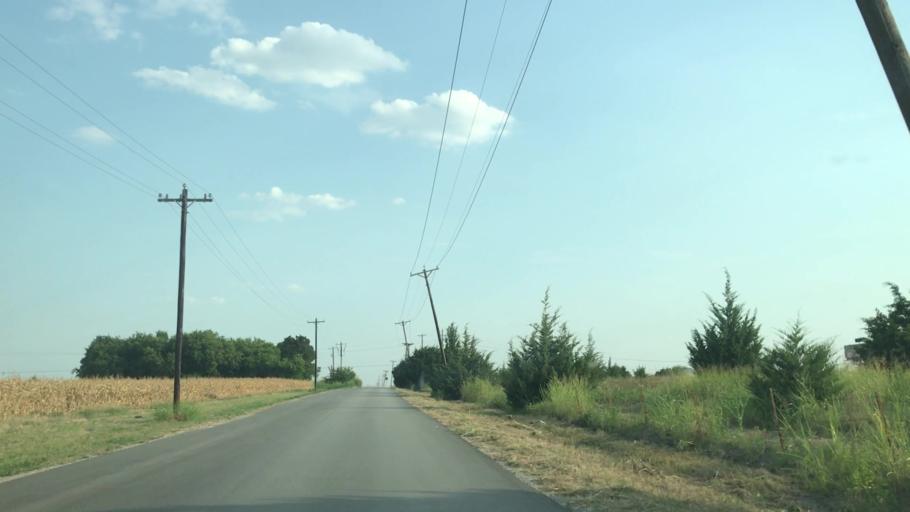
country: US
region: Texas
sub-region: Rockwall County
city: Fate
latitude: 32.9266
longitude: -96.4009
